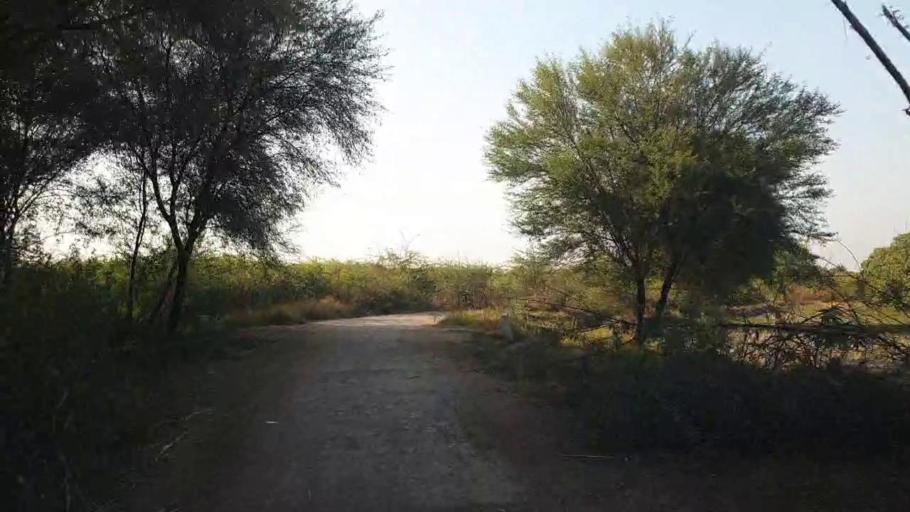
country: PK
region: Sindh
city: Mirpur Khas
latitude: 25.4358
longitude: 68.9103
